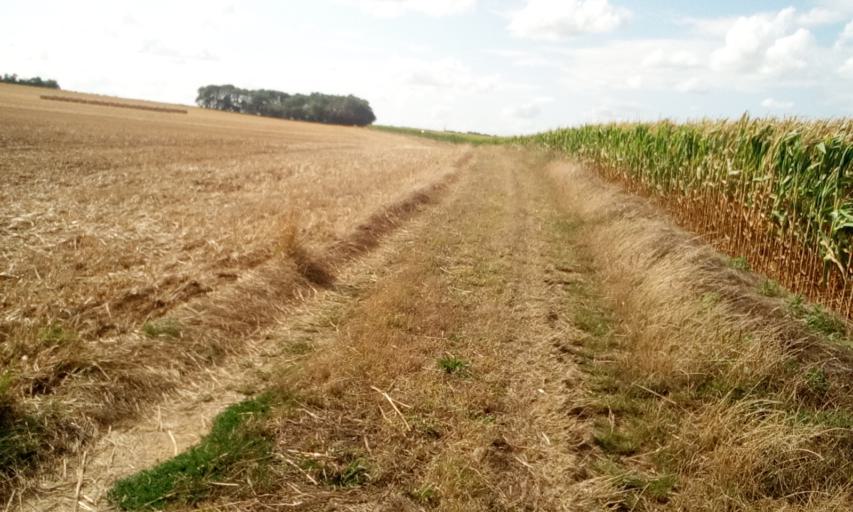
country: FR
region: Lower Normandy
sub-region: Departement du Calvados
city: Saint-Sylvain
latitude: 49.0711
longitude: -0.2428
